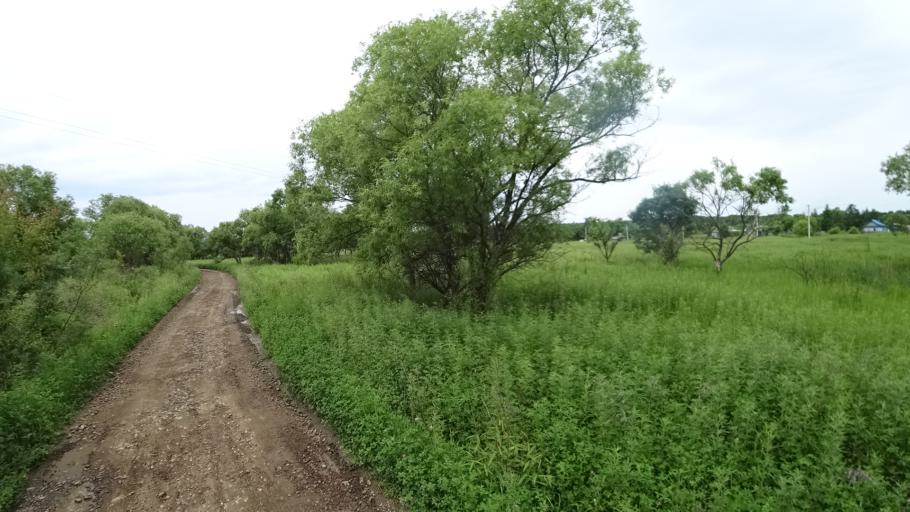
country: RU
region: Primorskiy
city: Novosysoyevka
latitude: 44.2090
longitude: 133.3283
